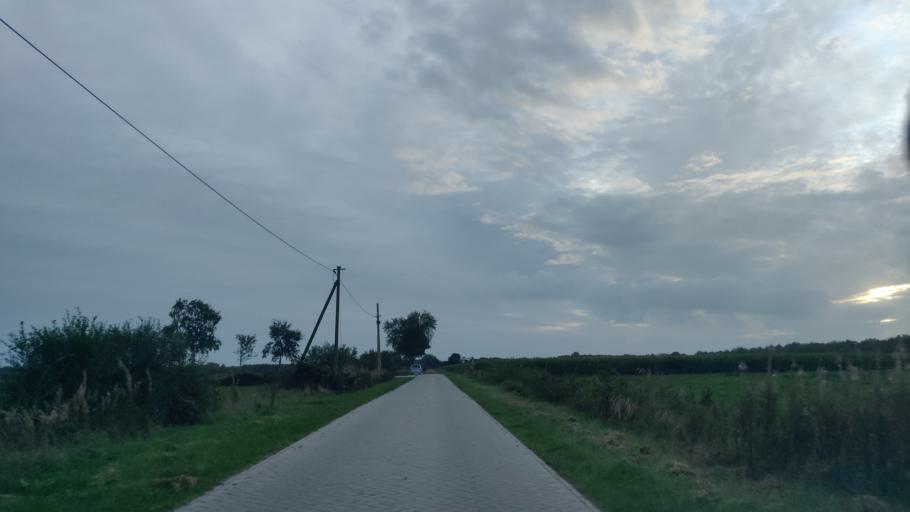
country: DE
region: Lower Saxony
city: Aurich
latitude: 53.5052
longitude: 7.4285
